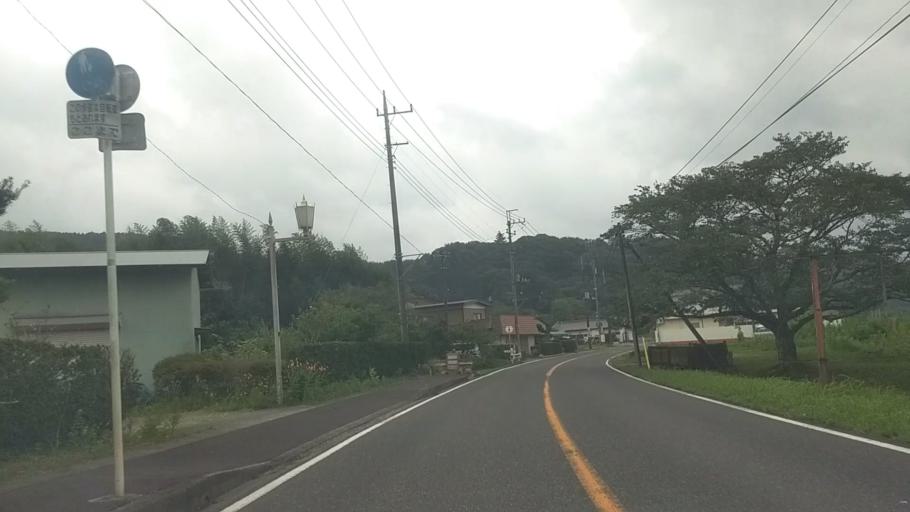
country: JP
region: Chiba
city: Kawaguchi
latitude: 35.2603
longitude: 140.0638
